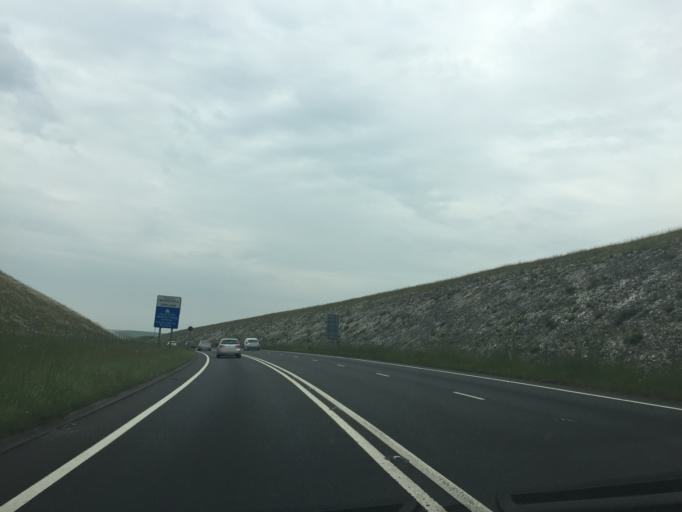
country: GB
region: England
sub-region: Dorset
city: Overcombe
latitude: 50.6713
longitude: -2.4662
